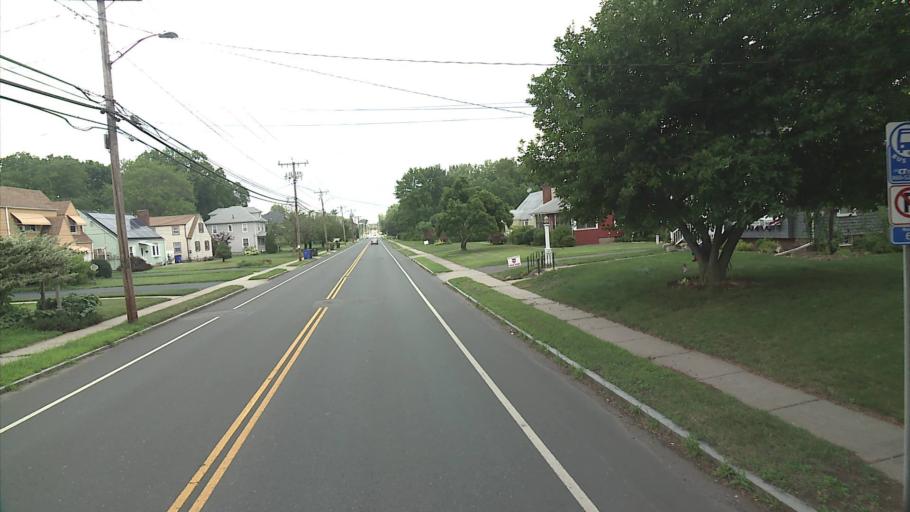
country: US
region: Connecticut
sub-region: Hartford County
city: Newington
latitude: 41.7240
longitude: -72.7350
